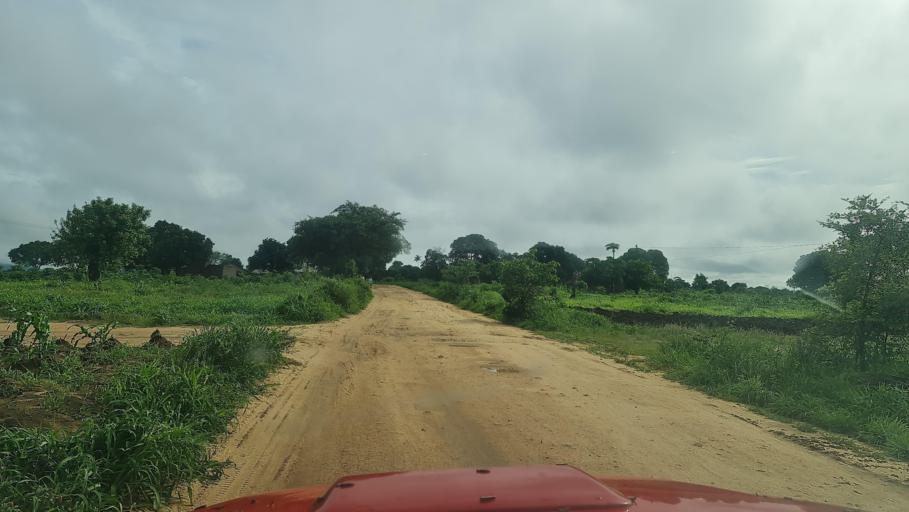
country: MW
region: Southern Region
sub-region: Nsanje District
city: Nsanje
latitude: -17.2914
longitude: 35.6006
